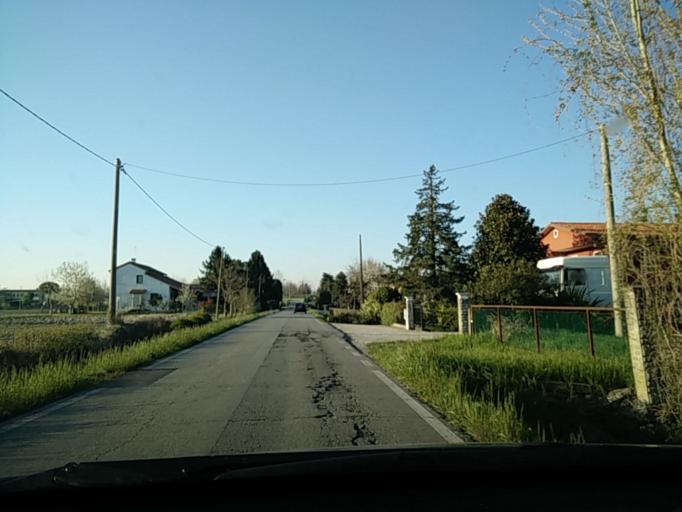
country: IT
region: Veneto
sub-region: Provincia di Venezia
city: San Dona di Piave
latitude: 45.6113
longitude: 12.5761
